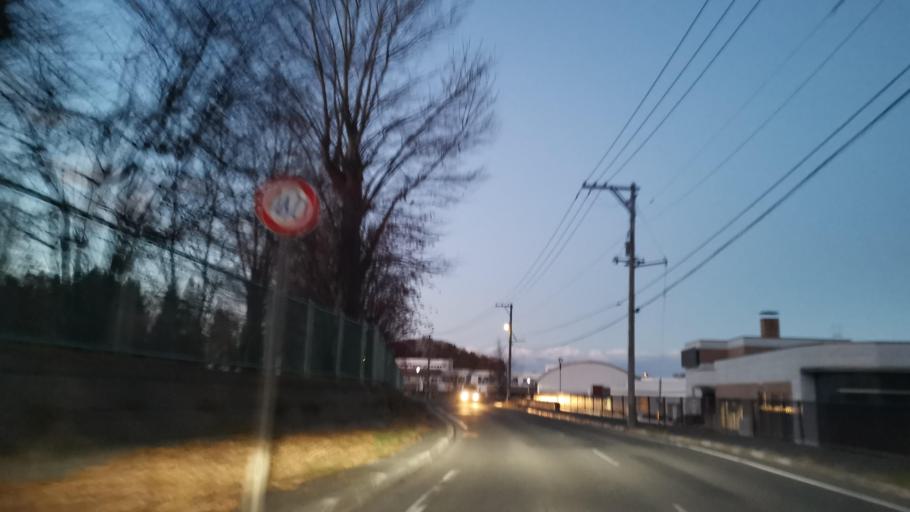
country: JP
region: Hokkaido
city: Sapporo
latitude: 42.9987
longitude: 141.3638
